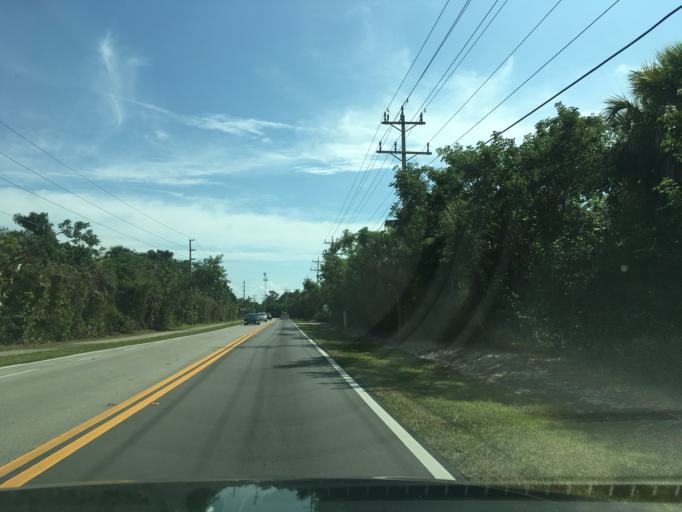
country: US
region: Florida
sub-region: Lee County
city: Saint James City
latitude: 26.4441
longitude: -82.1116
